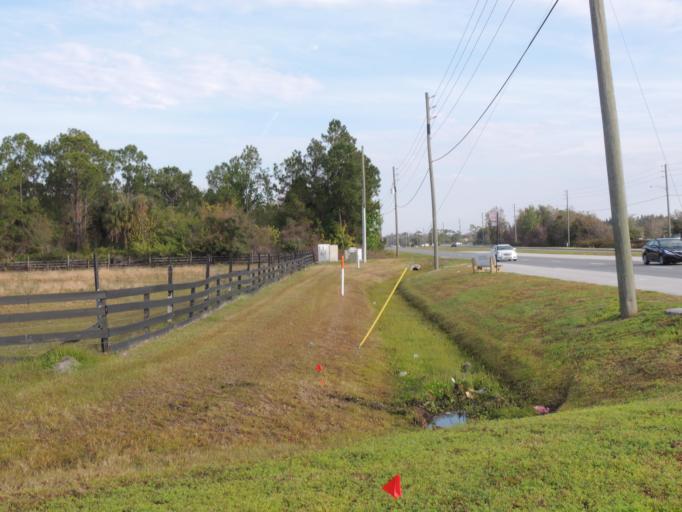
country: US
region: Florida
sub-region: Osceola County
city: Campbell
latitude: 28.2061
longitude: -81.4404
